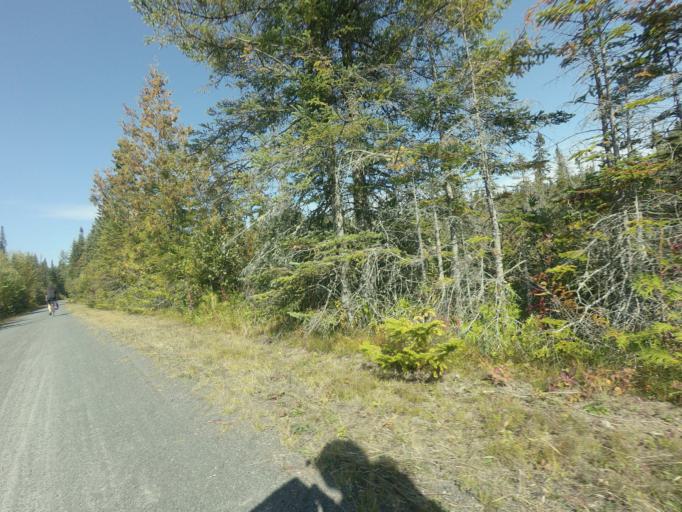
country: CA
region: Quebec
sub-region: Laurentides
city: Sainte-Agathe-des-Monts
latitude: 46.0892
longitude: -74.3436
